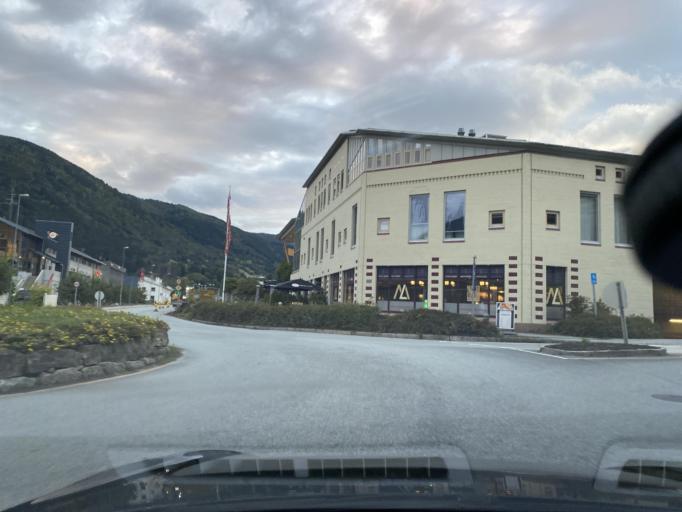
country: NO
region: Sogn og Fjordane
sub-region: Sogndal
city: Sogndalsfjora
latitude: 61.2324
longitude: 7.1070
